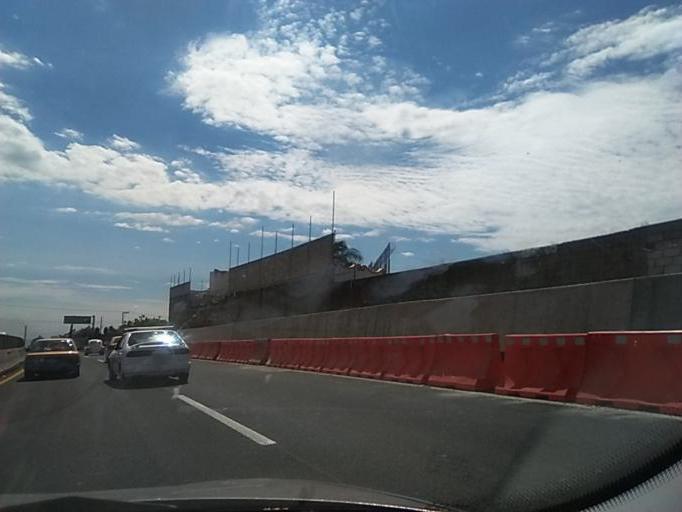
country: MX
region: Morelos
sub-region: Cuernavaca
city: Fraccionamiento Lomas de Ahuatlan
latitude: 18.9631
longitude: -99.2336
